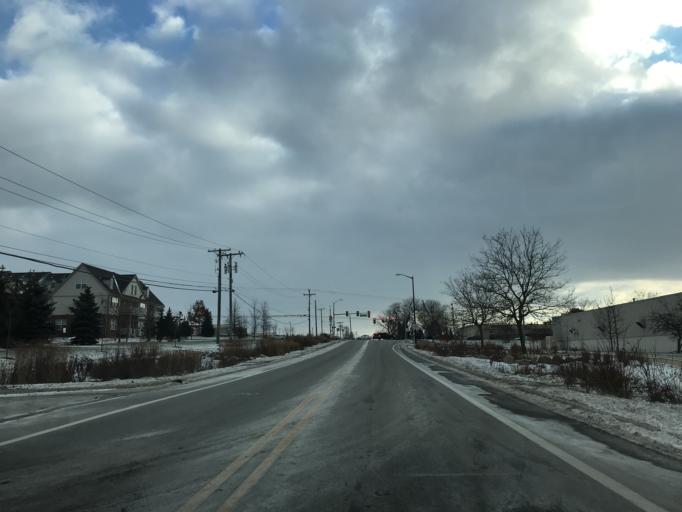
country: US
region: Michigan
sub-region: Washtenaw County
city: Ann Arbor
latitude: 42.2313
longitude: -83.7196
